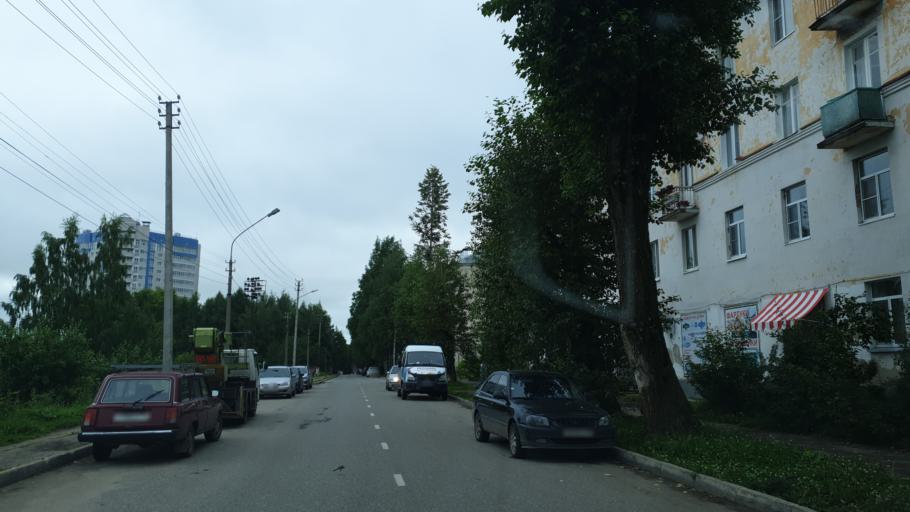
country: RU
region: Komi Republic
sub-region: Syktyvdinskiy Rayon
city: Syktyvkar
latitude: 61.6632
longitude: 50.8248
